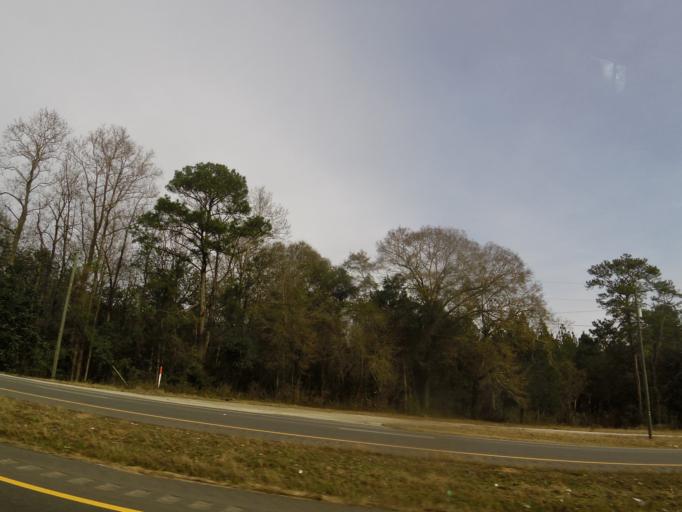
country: US
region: Alabama
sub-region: Dale County
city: Ozark
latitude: 31.5068
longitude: -85.6992
